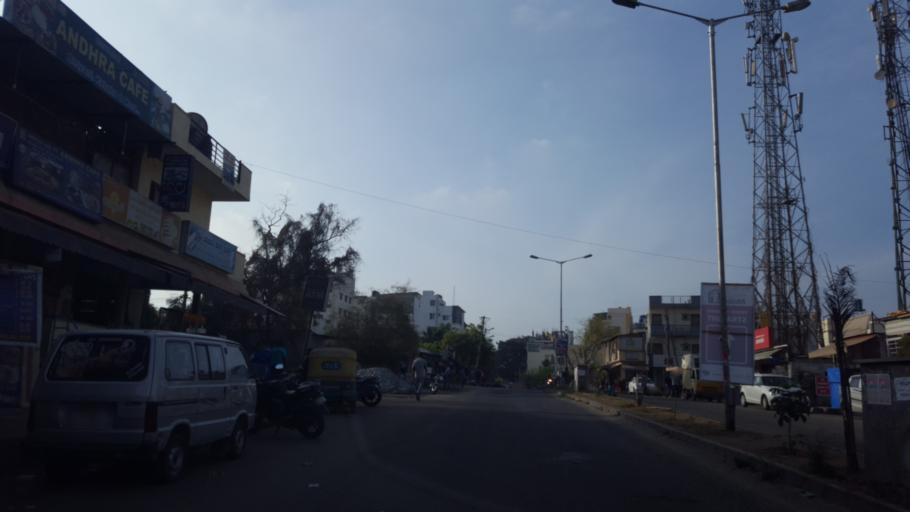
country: IN
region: Karnataka
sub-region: Bangalore Urban
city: Bangalore
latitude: 12.9175
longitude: 77.5001
